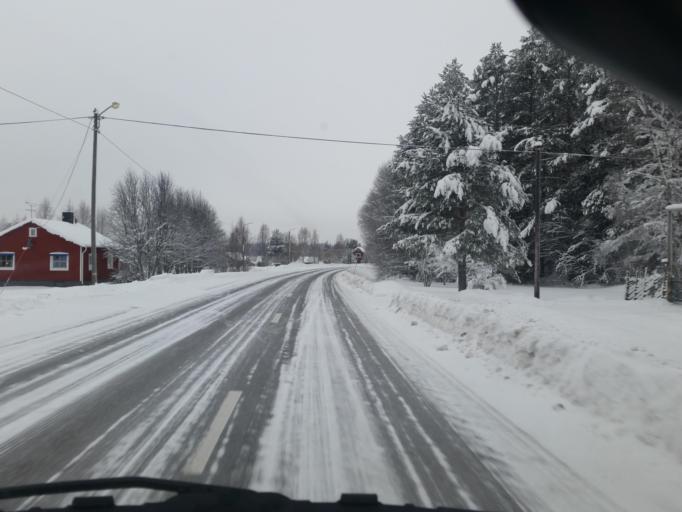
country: SE
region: Norrbotten
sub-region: Pitea Kommun
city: Roknas
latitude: 65.4276
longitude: 21.2782
